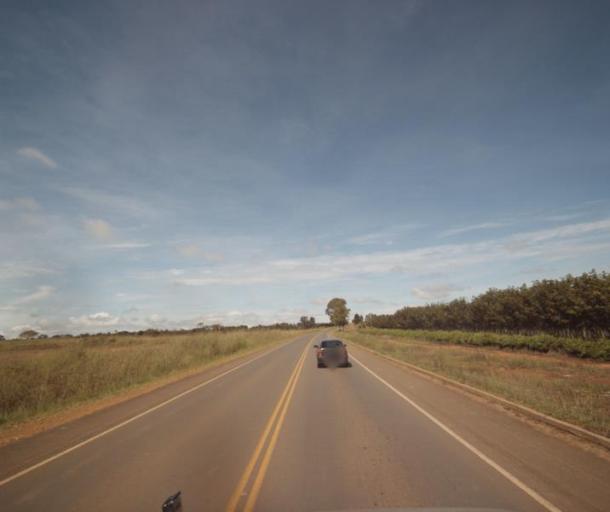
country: BR
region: Goias
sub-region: Anapolis
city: Anapolis
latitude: -16.1987
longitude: -48.9092
